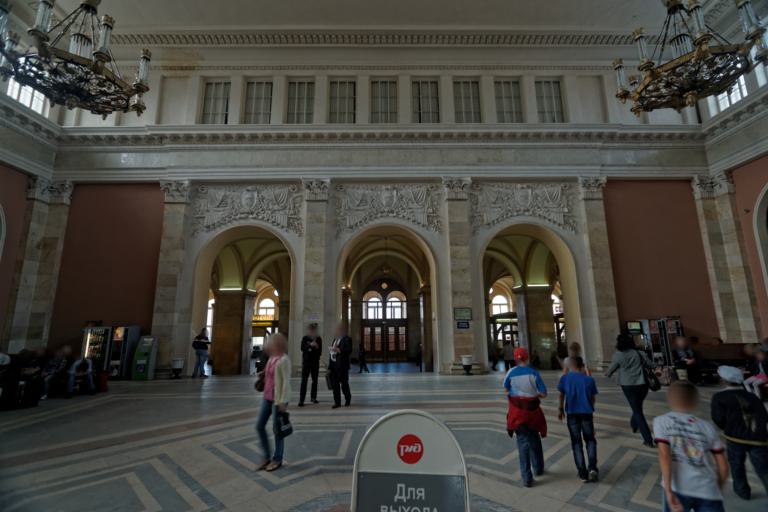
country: RU
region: St.-Petersburg
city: Centralniy
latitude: 59.9299
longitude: 30.3621
